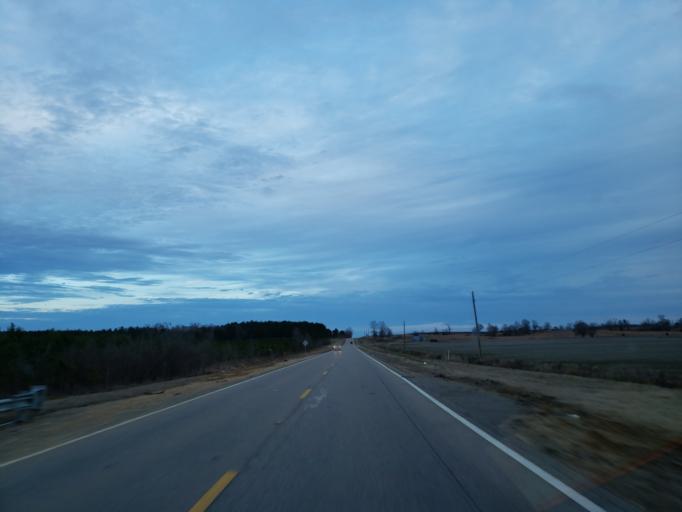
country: US
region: Mississippi
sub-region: Kemper County
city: De Kalb
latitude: 32.8309
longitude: -88.3956
